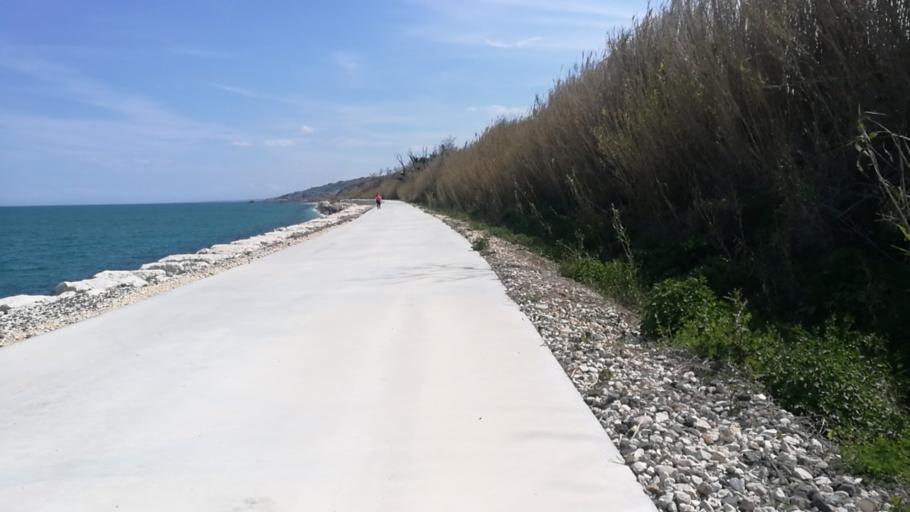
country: IT
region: Abruzzo
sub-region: Provincia di Chieti
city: Marina di San Vito
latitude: 42.3260
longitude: 14.4254
